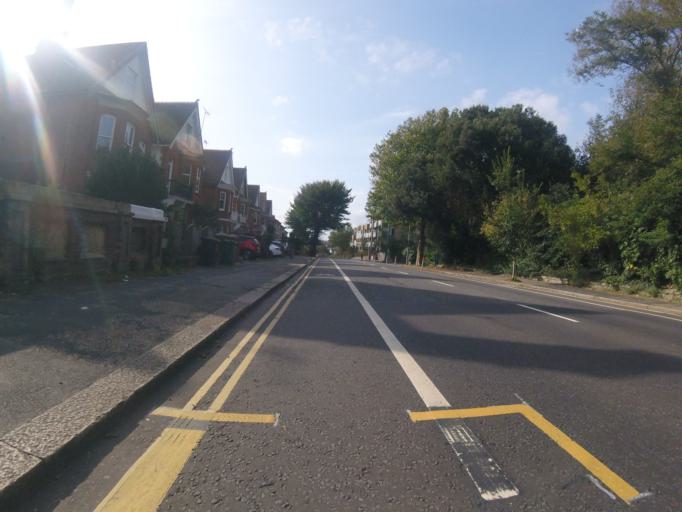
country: GB
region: England
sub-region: Brighton and Hove
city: Hove
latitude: 50.8385
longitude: -0.1696
